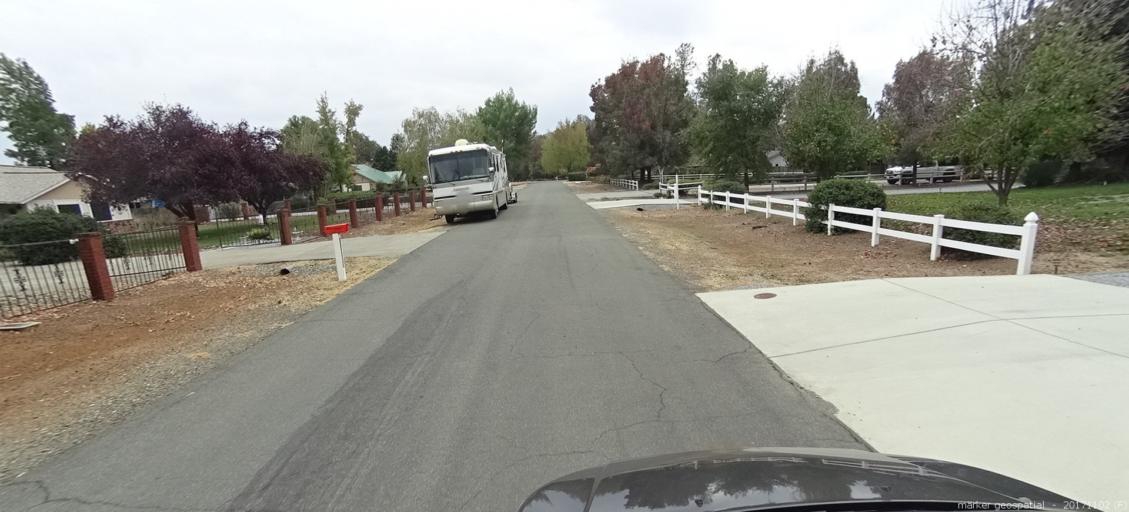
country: US
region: California
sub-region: Shasta County
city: Shasta Lake
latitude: 40.6576
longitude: -122.3274
